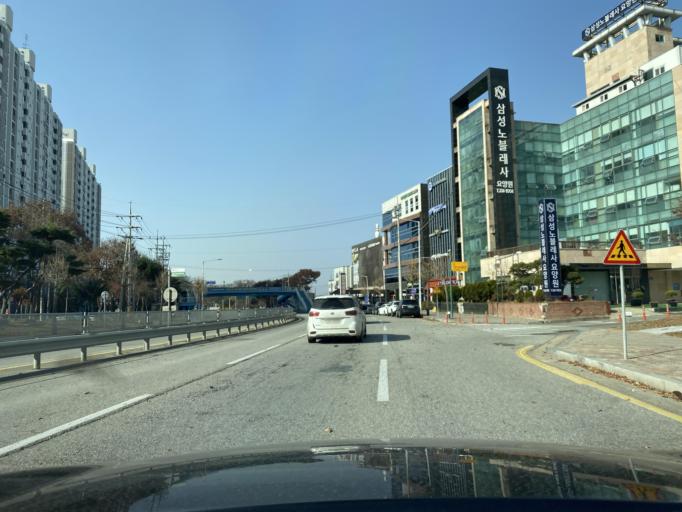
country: KR
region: Chungcheongnam-do
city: Yesan
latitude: 36.6935
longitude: 126.8340
